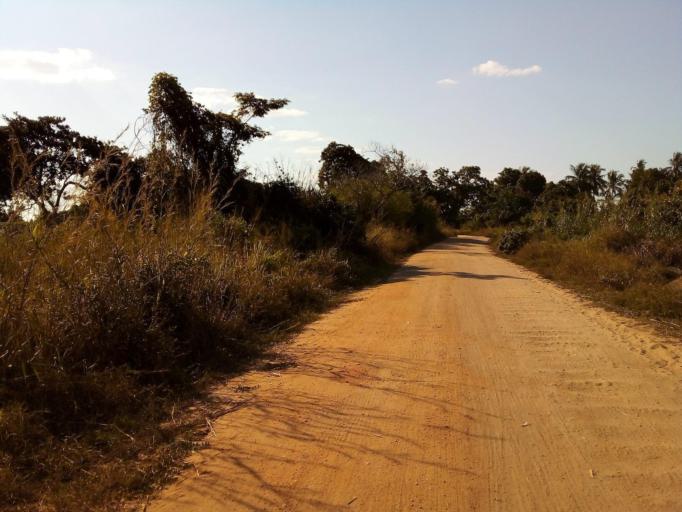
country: MZ
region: Zambezia
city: Quelimane
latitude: -17.5735
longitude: 36.6402
